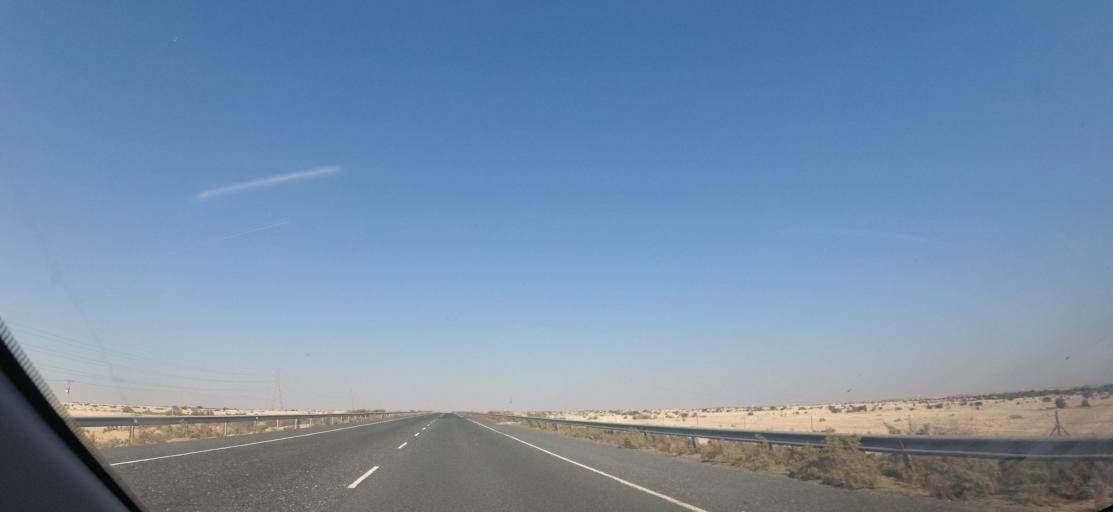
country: QA
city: Al Jumayliyah
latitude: 25.5865
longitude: 51.0610
